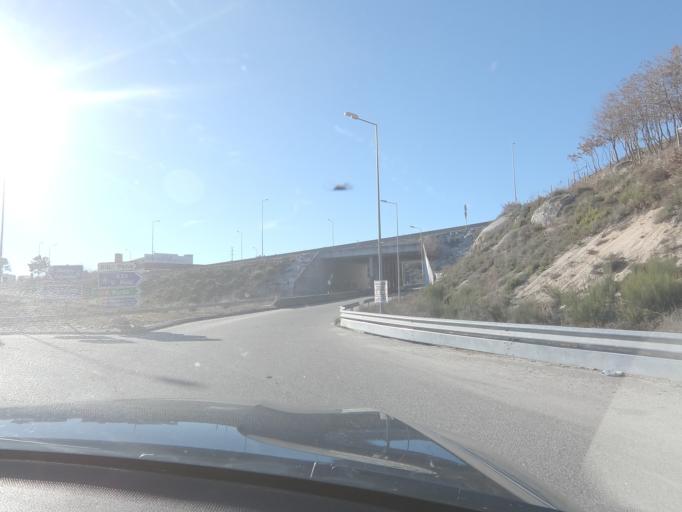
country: PT
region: Vila Real
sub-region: Vila Pouca de Aguiar
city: Vila Pouca de Aguiar
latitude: 41.4909
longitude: -7.6593
